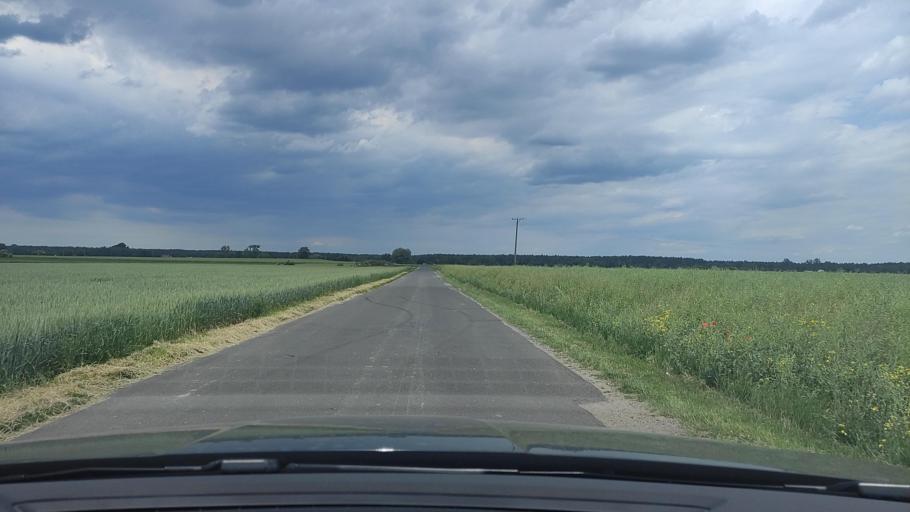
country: PL
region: Greater Poland Voivodeship
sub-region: Powiat poznanski
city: Kostrzyn
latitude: 52.4844
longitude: 17.1912
